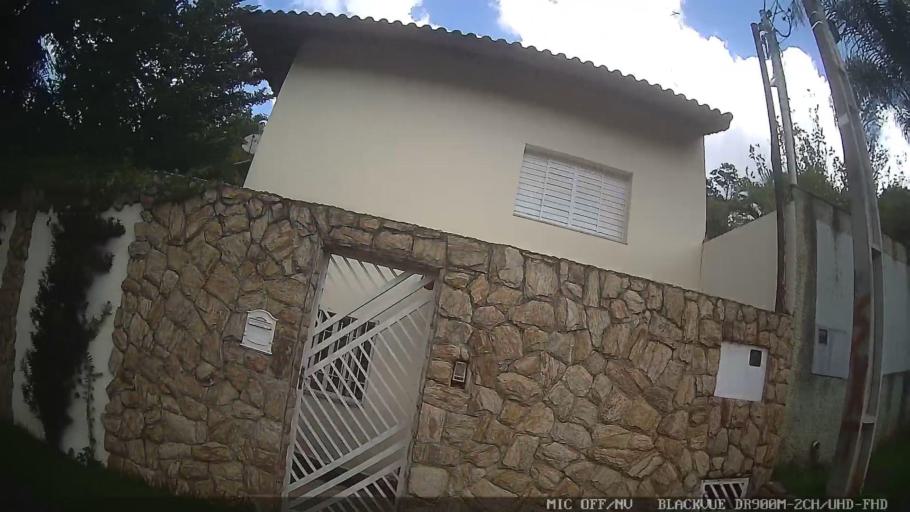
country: BR
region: Minas Gerais
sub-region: Extrema
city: Extrema
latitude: -22.8607
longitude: -46.3129
